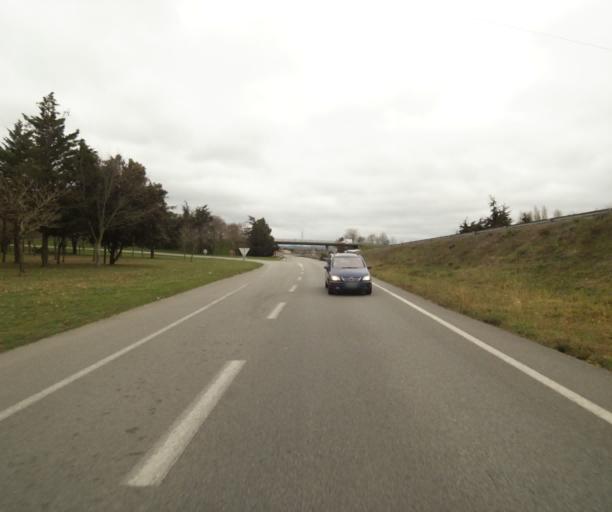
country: FR
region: Midi-Pyrenees
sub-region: Departement de l'Ariege
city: Pamiers
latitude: 43.1333
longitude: 1.6257
